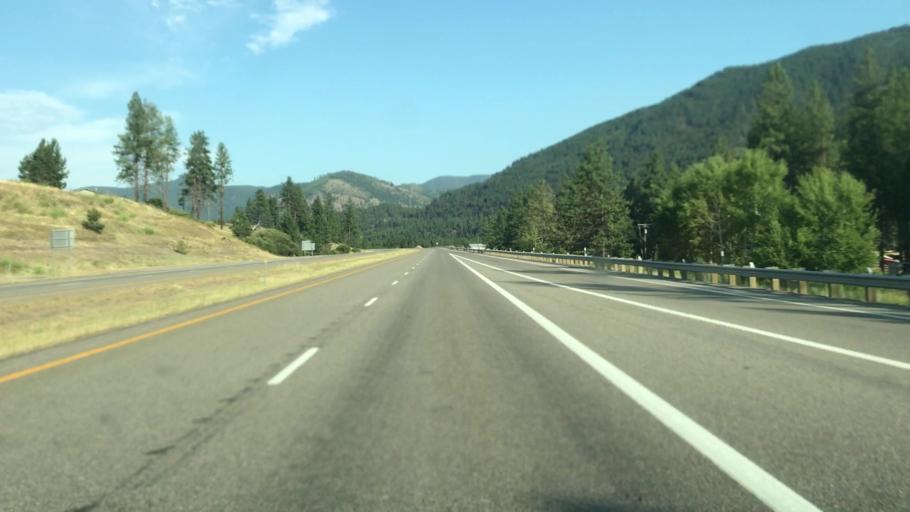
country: US
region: Montana
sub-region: Missoula County
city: Frenchtown
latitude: 47.0045
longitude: -114.4916
